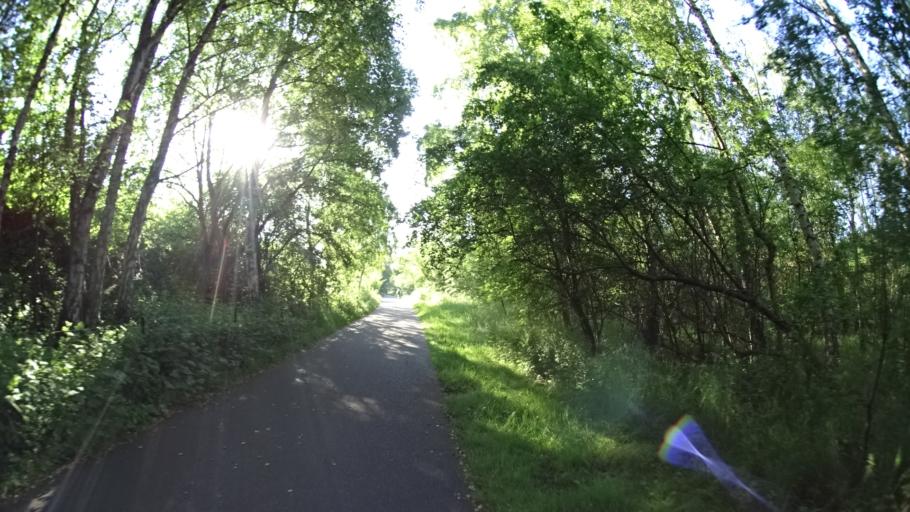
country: DK
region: Central Jutland
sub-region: Arhus Kommune
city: Stavtrup
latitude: 56.1428
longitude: 10.1653
